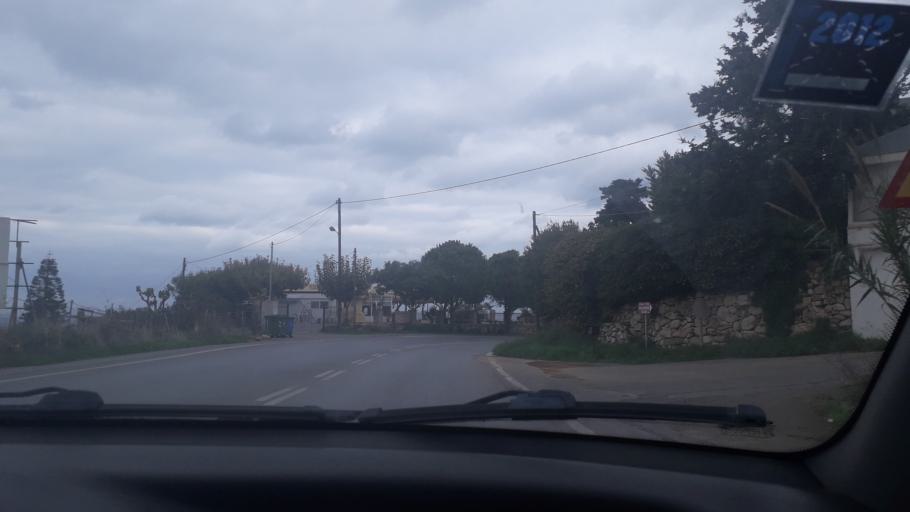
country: GR
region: Crete
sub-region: Nomos Rethymnis
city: Rethymno
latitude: 35.3583
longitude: 24.4679
